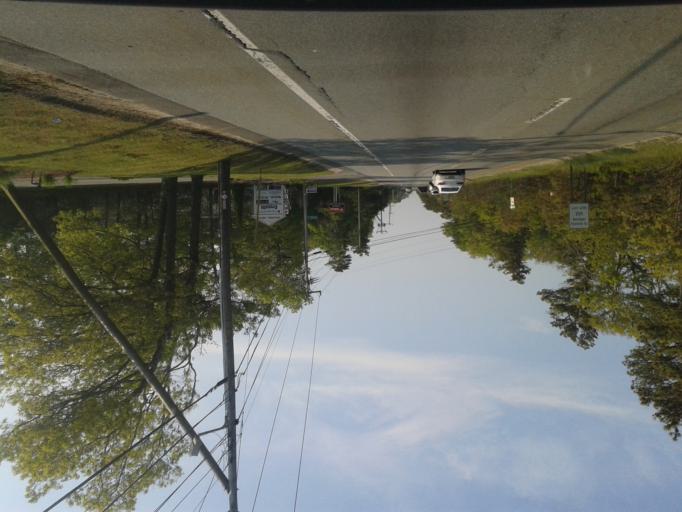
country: US
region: Massachusetts
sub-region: Barnstable County
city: Bourne
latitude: 41.7323
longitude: -70.5844
